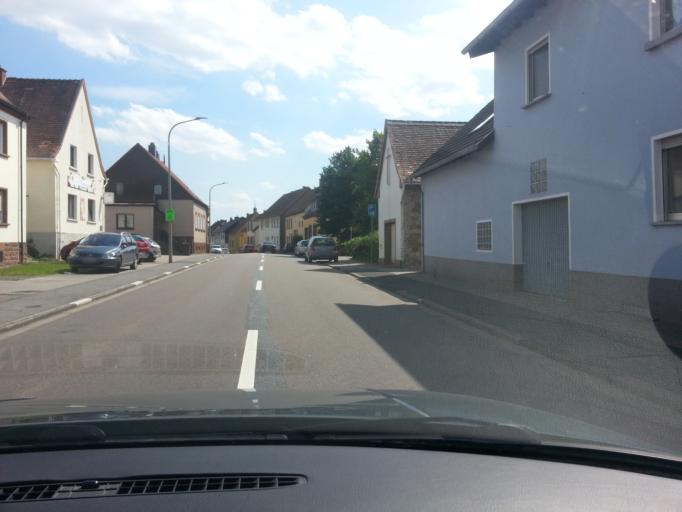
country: DE
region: Saarland
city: Blieskastel
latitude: 49.2309
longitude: 7.2674
